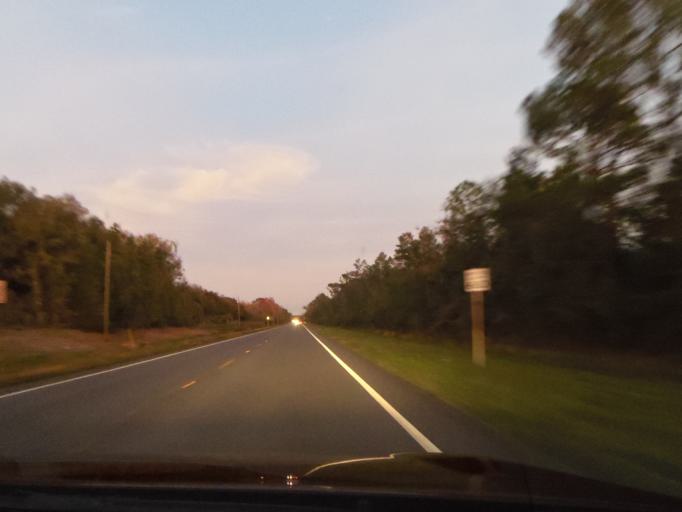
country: US
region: Florida
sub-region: Volusia County
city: De Leon Springs
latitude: 29.2260
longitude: -81.3171
